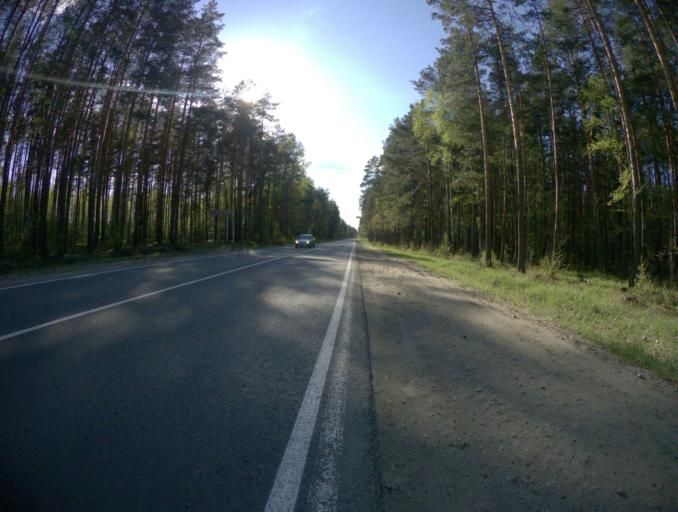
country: RU
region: Vladimir
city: Raduzhnyy
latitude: 56.0304
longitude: 40.3751
